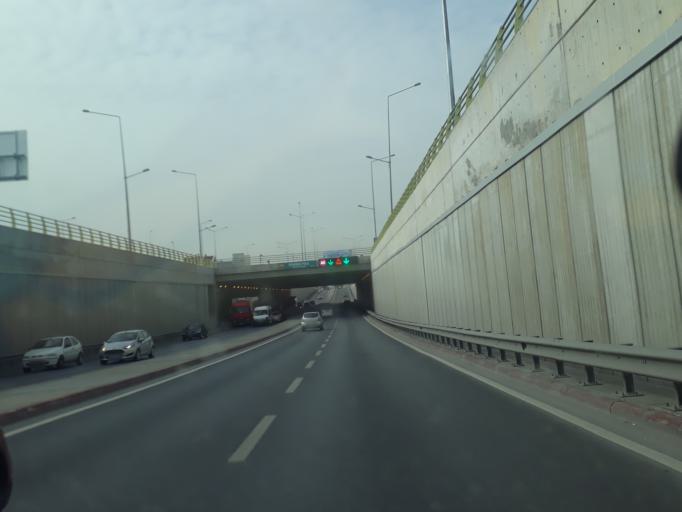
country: TR
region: Konya
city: Selcuklu
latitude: 37.9597
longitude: 32.5143
